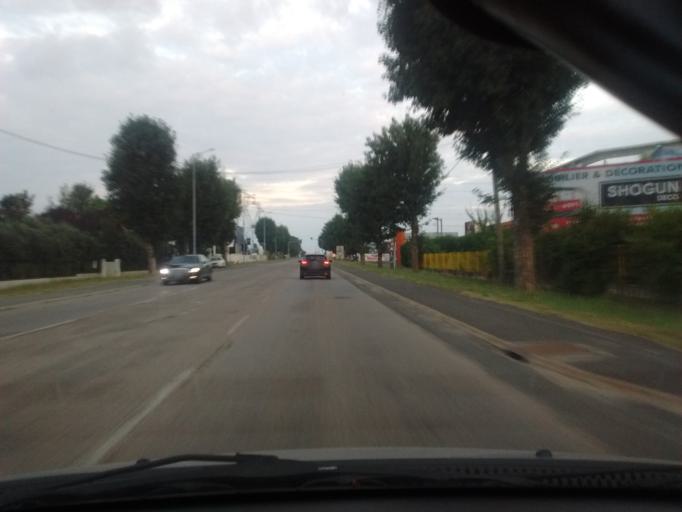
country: FR
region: Ile-de-France
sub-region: Departement de Seine-et-Marne
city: Pringy
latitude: 48.5182
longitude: 2.5643
